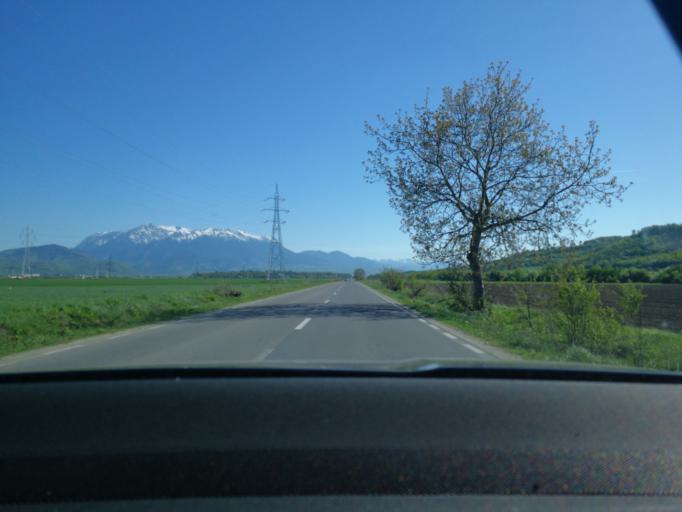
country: RO
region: Brasov
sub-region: Comuna Vulcan
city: Vulcan
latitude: 45.6153
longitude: 25.4238
